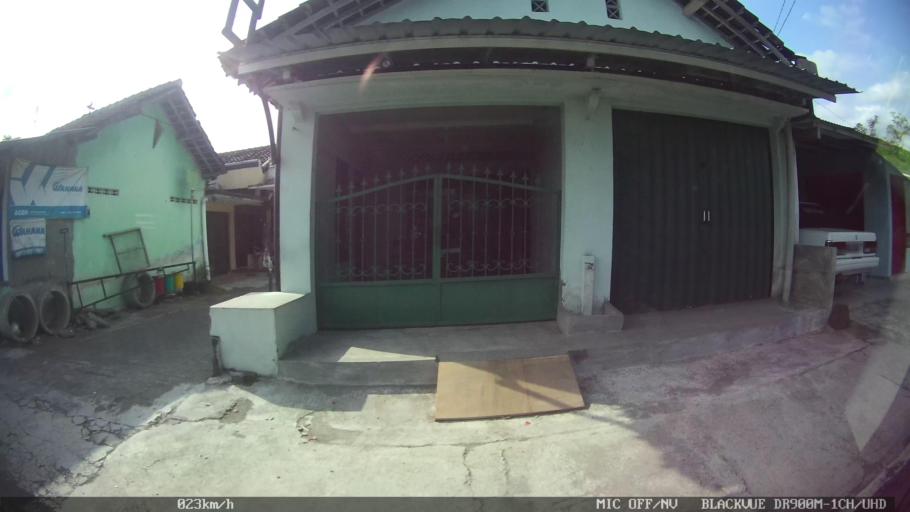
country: ID
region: Daerah Istimewa Yogyakarta
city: Depok
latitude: -7.7228
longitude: 110.4361
